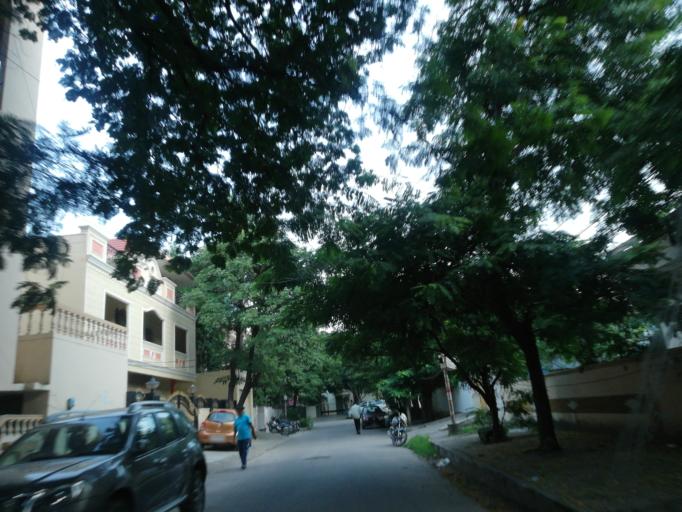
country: IN
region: Telangana
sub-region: Rangareddi
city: Kukatpalli
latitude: 17.4498
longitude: 78.4388
